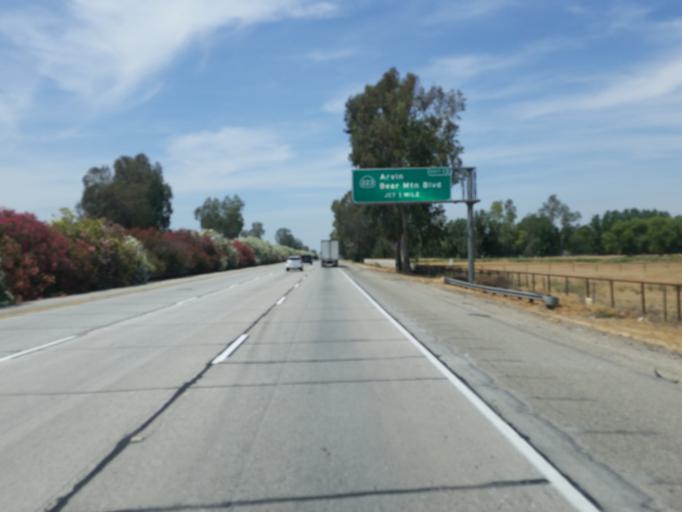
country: US
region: California
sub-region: Kern County
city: Greenfield
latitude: 35.1908
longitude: -119.0073
